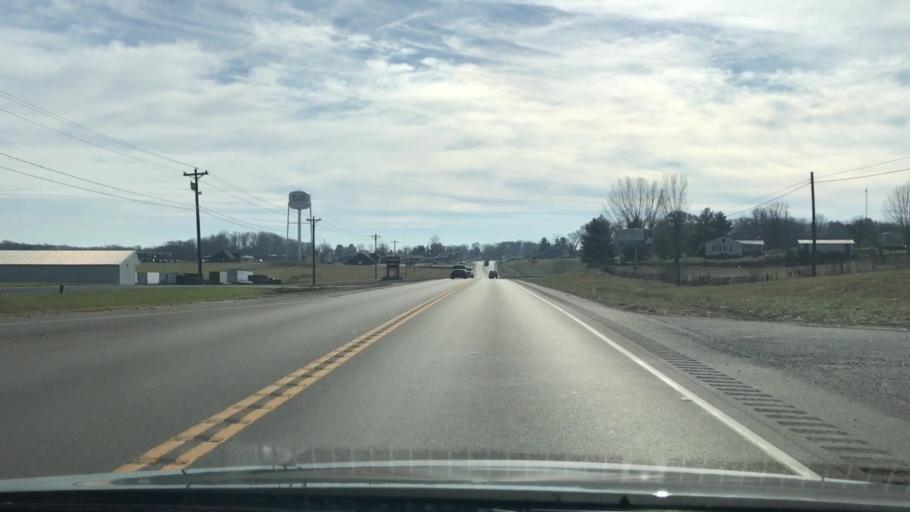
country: US
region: Kentucky
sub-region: Monroe County
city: Tompkinsville
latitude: 36.7303
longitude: -85.6876
